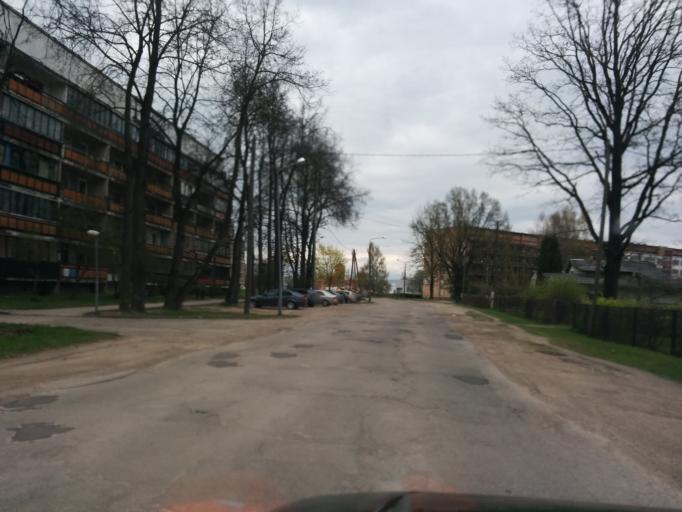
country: LV
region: Ozolnieku
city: Ozolnieki
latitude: 56.6671
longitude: 23.7602
